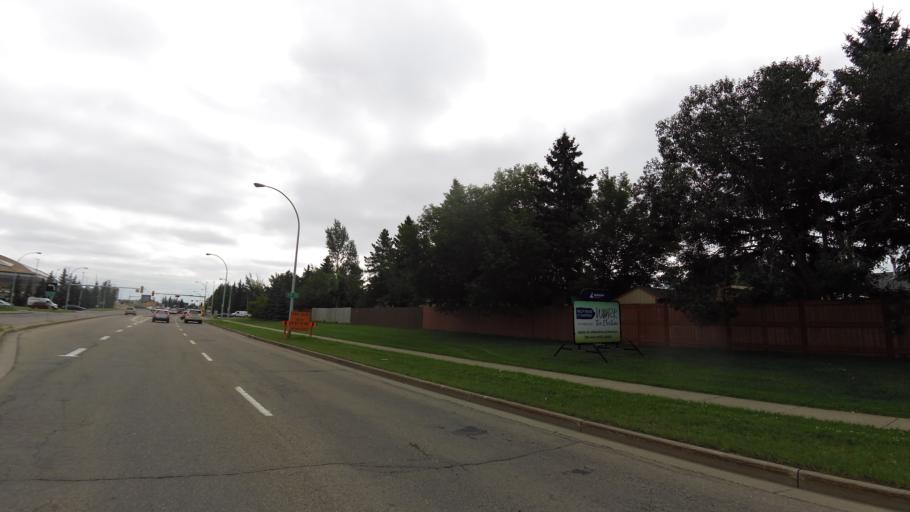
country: CA
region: Alberta
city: St. Albert
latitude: 53.5214
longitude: -113.6329
